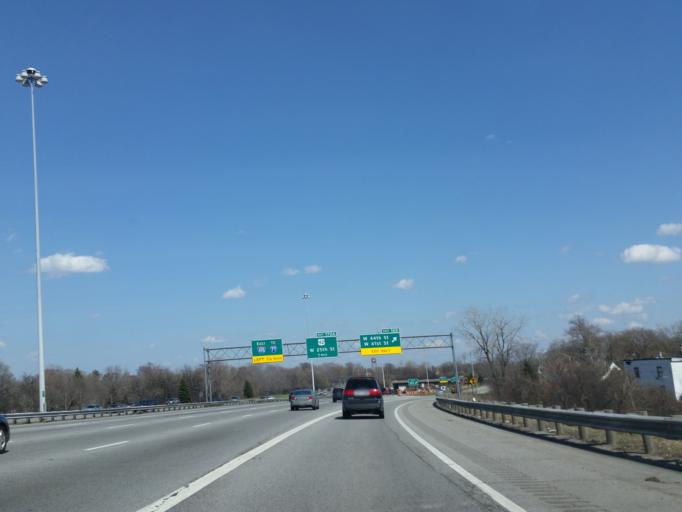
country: US
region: Ohio
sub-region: Cuyahoga County
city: Cleveland
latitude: 41.4746
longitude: -81.7224
